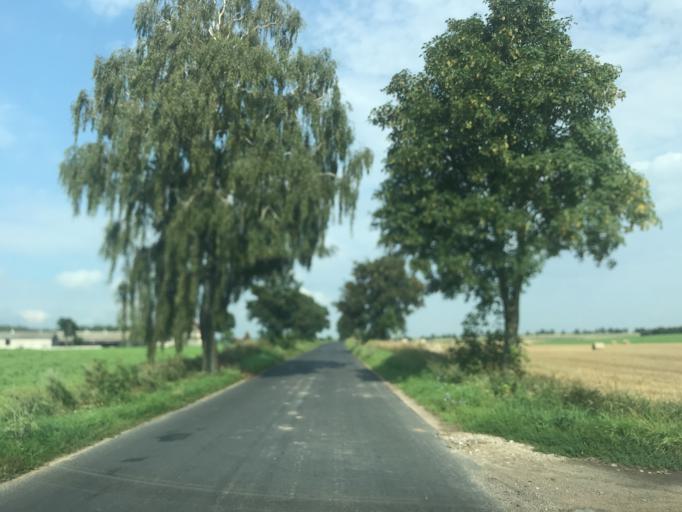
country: PL
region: Warmian-Masurian Voivodeship
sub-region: Powiat nowomiejski
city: Kurzetnik
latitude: 53.3662
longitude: 19.5880
